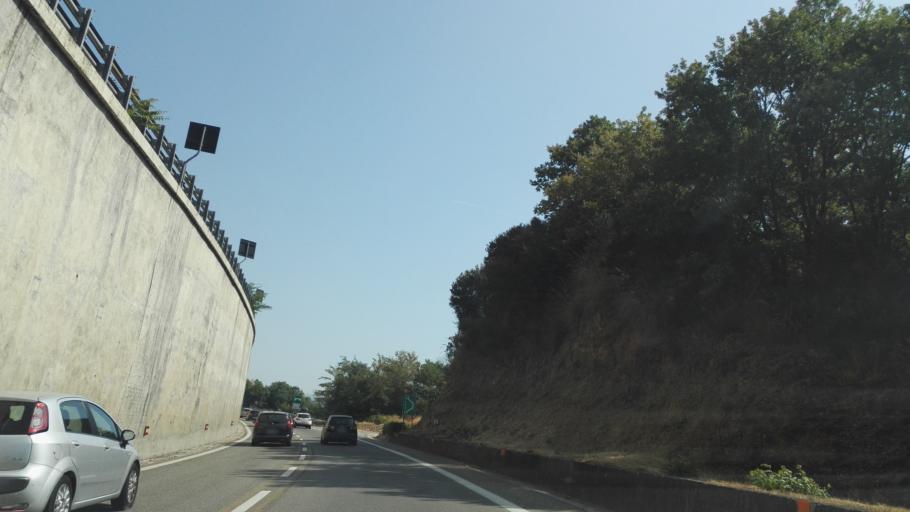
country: IT
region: Calabria
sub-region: Provincia di Cosenza
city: Altilia
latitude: 39.1344
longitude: 16.2716
